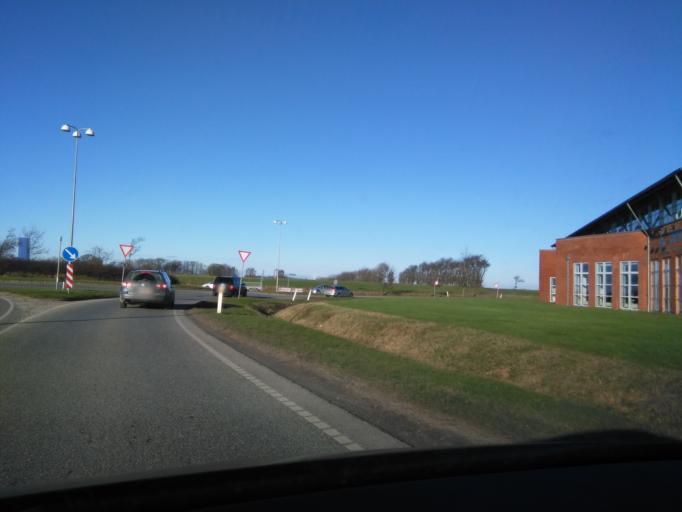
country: DK
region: North Denmark
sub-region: Mariagerfjord Kommune
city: Hobro
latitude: 56.6542
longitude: 9.7948
